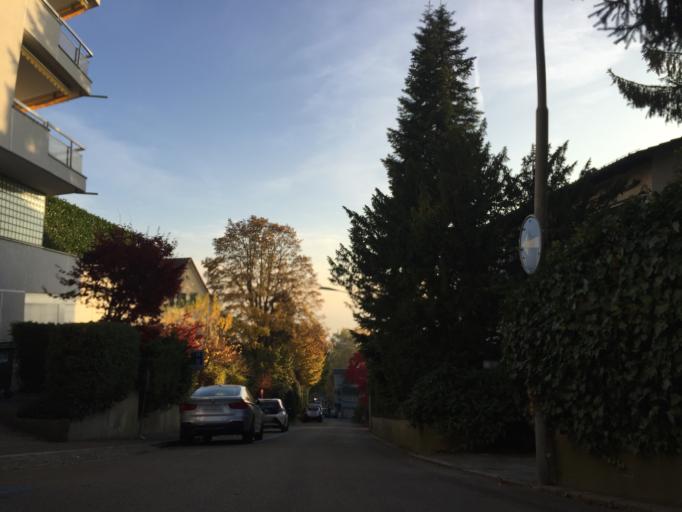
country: CH
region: Zurich
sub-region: Bezirk Zuerich
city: Zuerich (Kreis 7) / Fluntern
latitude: 47.3830
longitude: 8.5573
